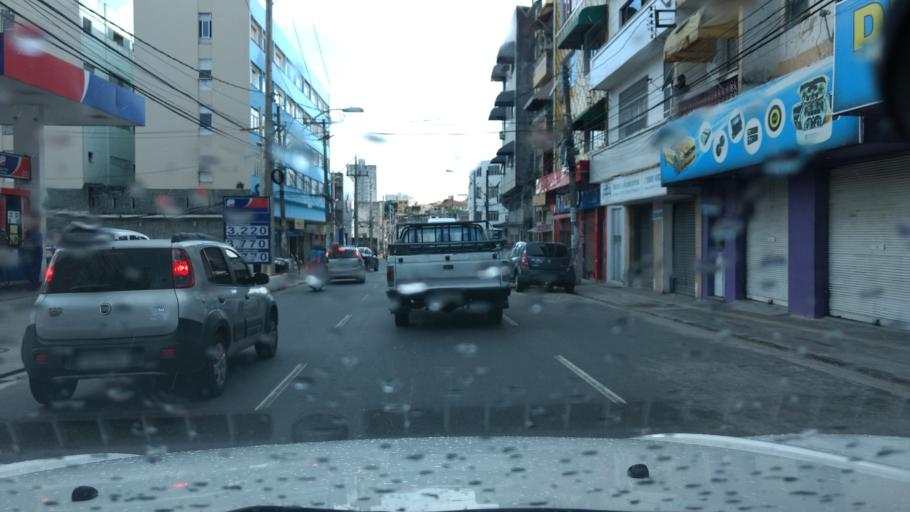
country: BR
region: Bahia
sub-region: Salvador
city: Salvador
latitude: -12.9741
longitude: -38.4998
